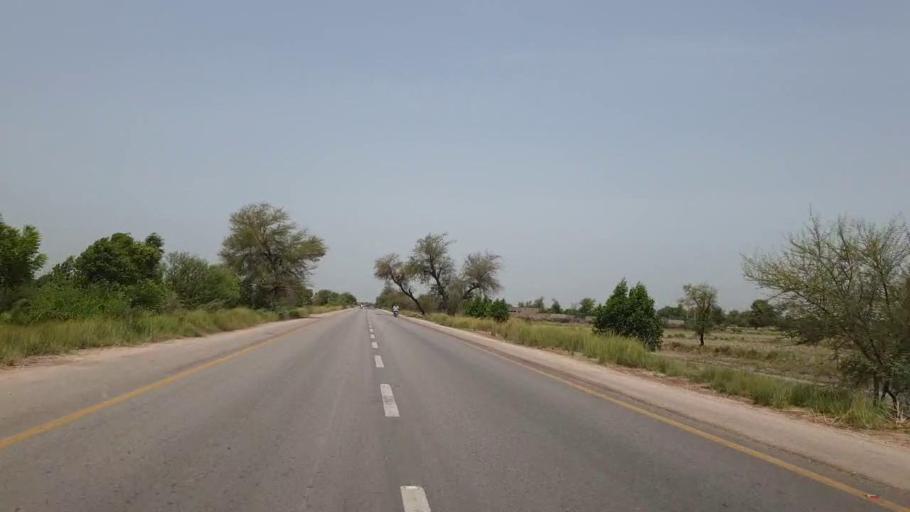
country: PK
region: Sindh
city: Nawabshah
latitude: 26.2125
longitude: 68.5150
